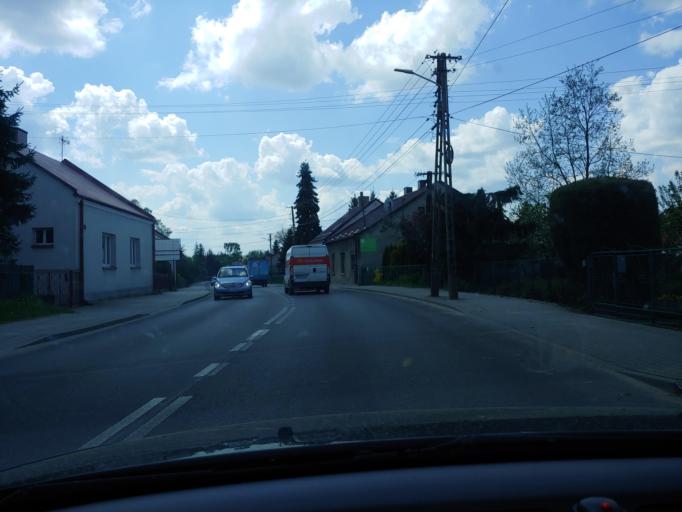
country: PL
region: Subcarpathian Voivodeship
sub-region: Powiat mielecki
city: Radomysl Wielki
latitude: 50.1945
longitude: 21.2741
